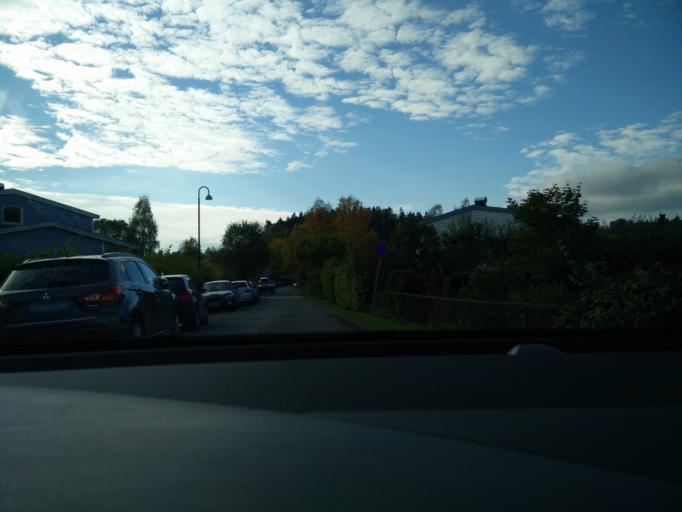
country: NO
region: Akershus
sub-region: Baerum
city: Lysaker
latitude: 59.9376
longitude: 10.6132
